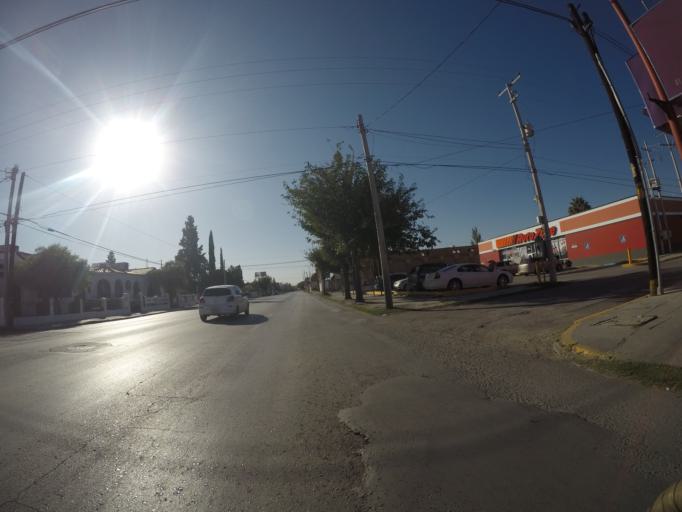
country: MX
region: Chihuahua
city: Ciudad Juarez
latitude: 31.7381
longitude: -106.4656
